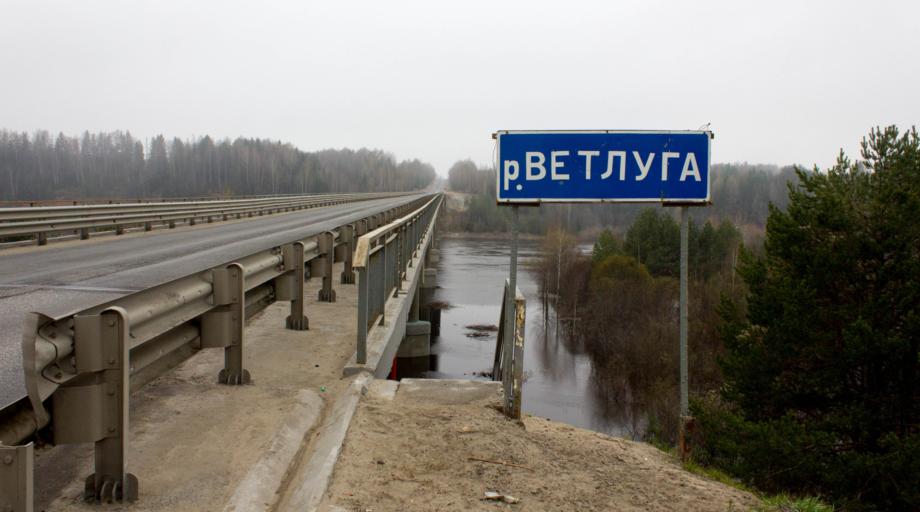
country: RU
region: Nizjnij Novgorod
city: Krasnyye Baki
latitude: 57.1097
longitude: 45.1919
